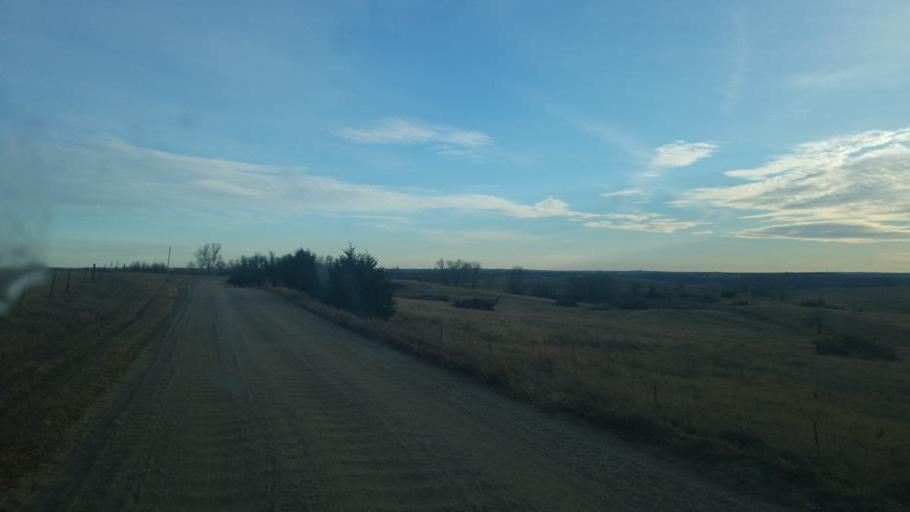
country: US
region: Nebraska
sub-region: Knox County
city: Center
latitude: 42.6979
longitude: -97.8498
